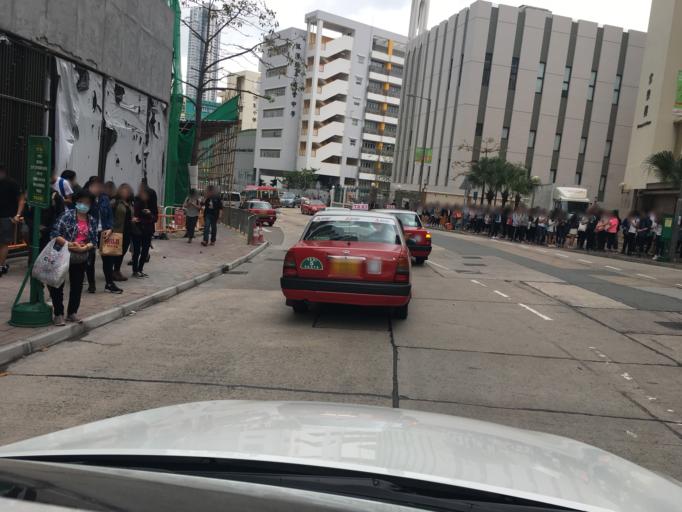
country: HK
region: Kowloon City
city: Kowloon
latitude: 22.3197
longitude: 114.1818
